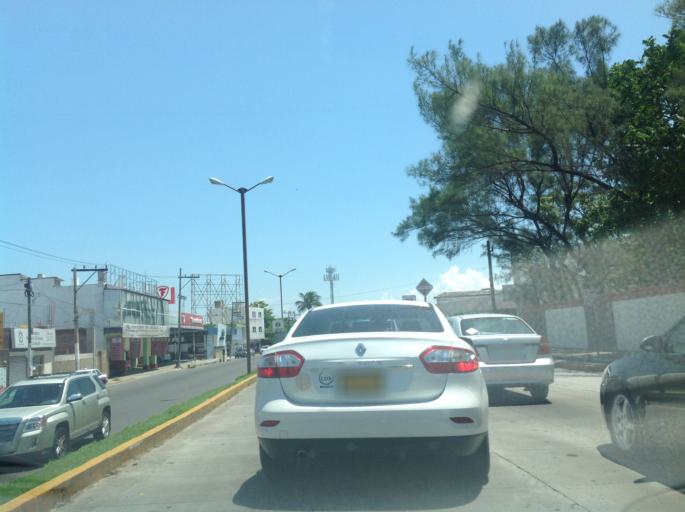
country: MX
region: Veracruz
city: Veracruz
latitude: 19.1546
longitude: -96.1305
